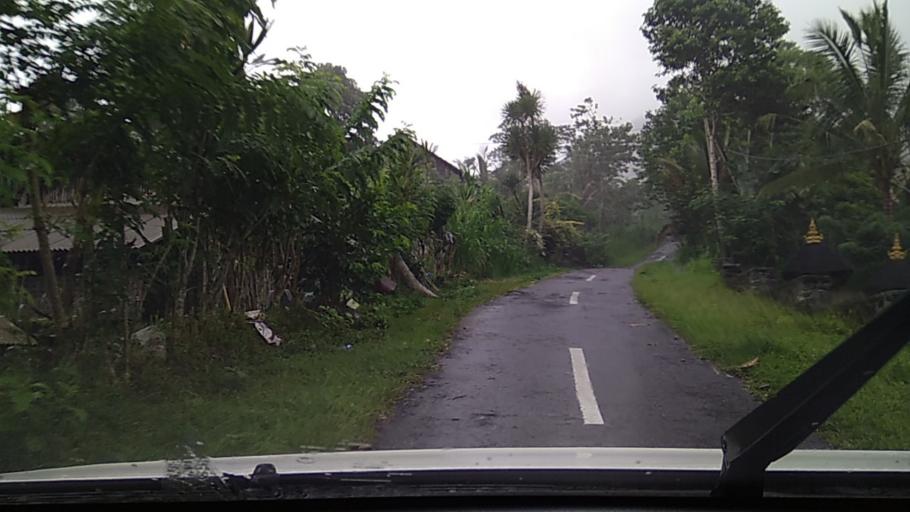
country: ID
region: Bali
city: Tiyingtali Kelod
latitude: -8.3984
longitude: 115.6319
